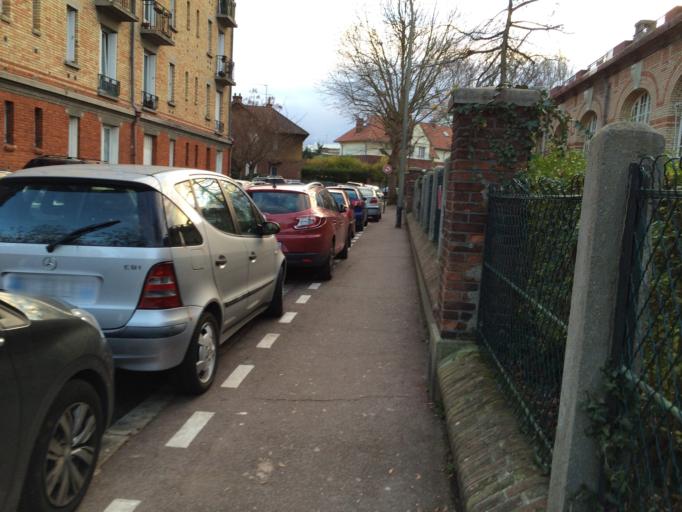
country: FR
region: Ile-de-France
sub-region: Departement des Hauts-de-Seine
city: Saint-Cloud
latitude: 48.8626
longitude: 2.2100
